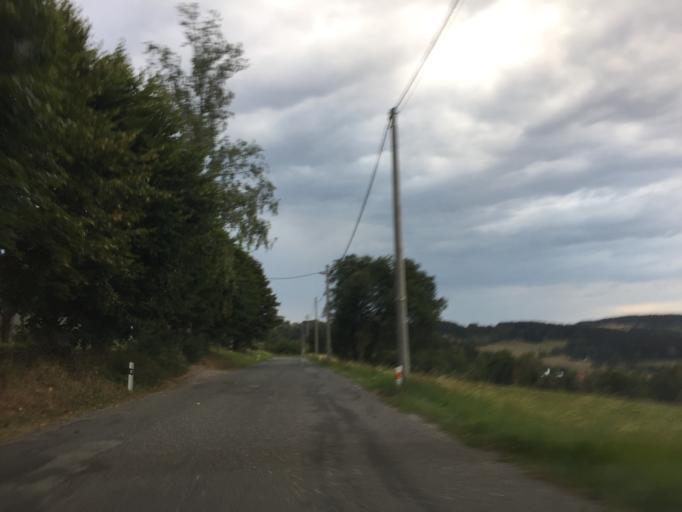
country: CZ
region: Liberecky
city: Mala Skala
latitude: 50.6599
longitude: 15.1942
